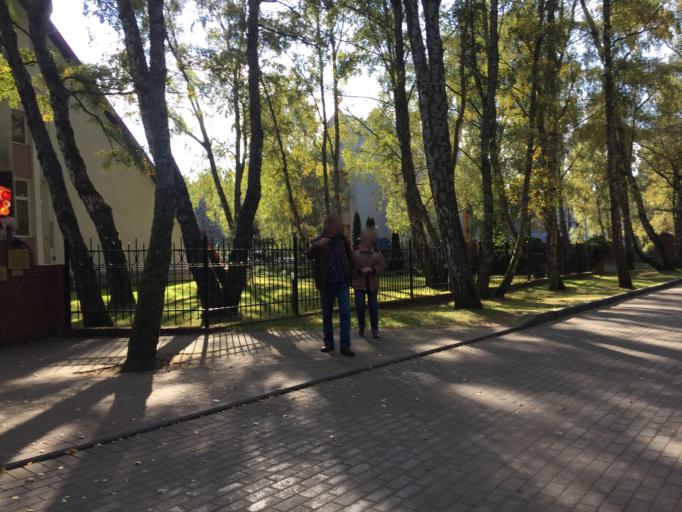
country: RU
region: Kaliningrad
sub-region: Gorod Svetlogorsk
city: Svetlogorsk
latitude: 54.9466
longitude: 20.1651
